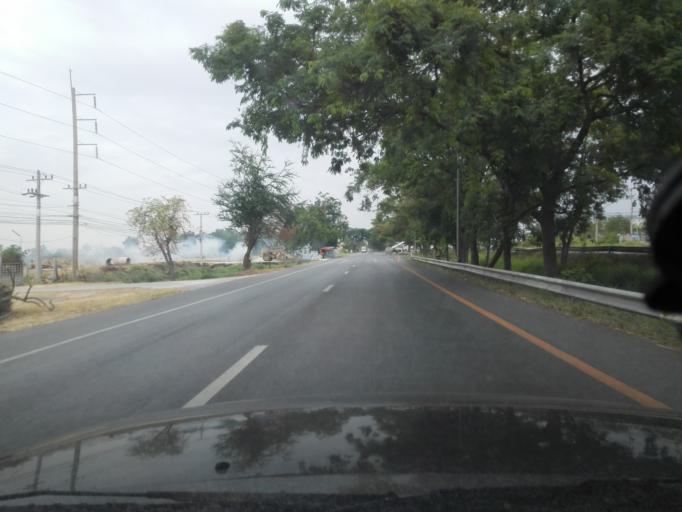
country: TH
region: Nakhon Sawan
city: Nakhon Sawan
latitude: 15.7334
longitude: 100.0287
